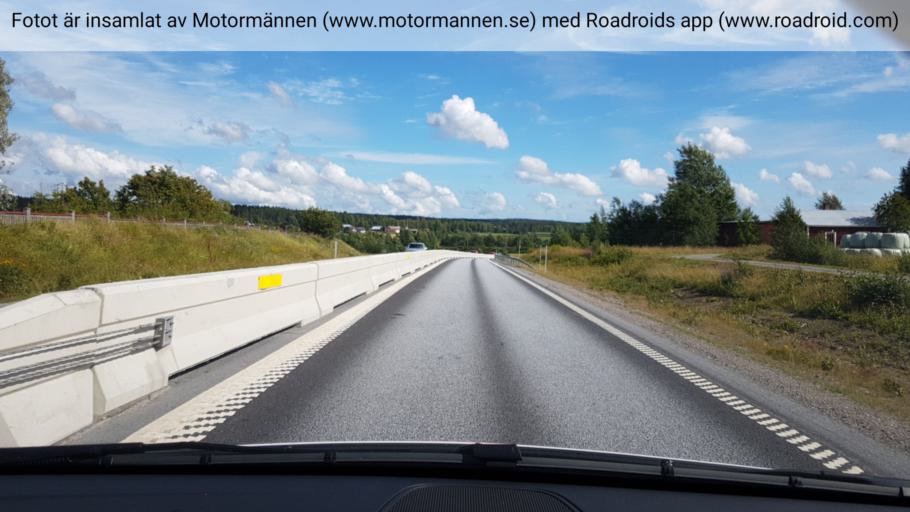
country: SE
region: Vaesterbotten
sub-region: Umea Kommun
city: Roback
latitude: 63.8869
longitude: 20.0189
